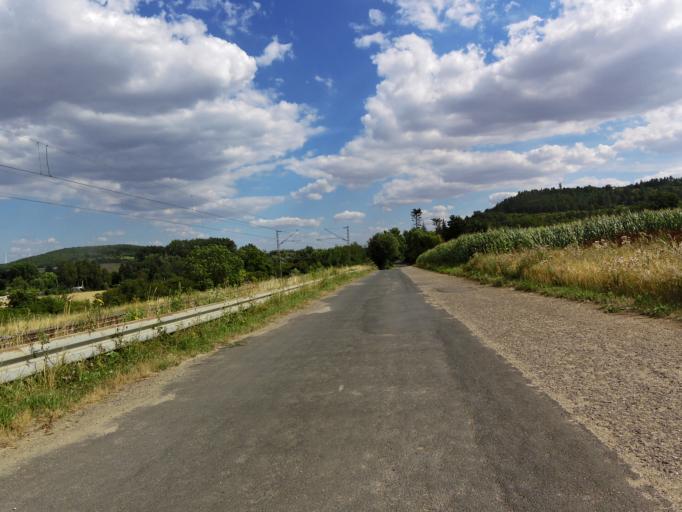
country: DE
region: Bavaria
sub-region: Regierungsbezirk Unterfranken
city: Randersacker
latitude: 49.7449
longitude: 9.9805
